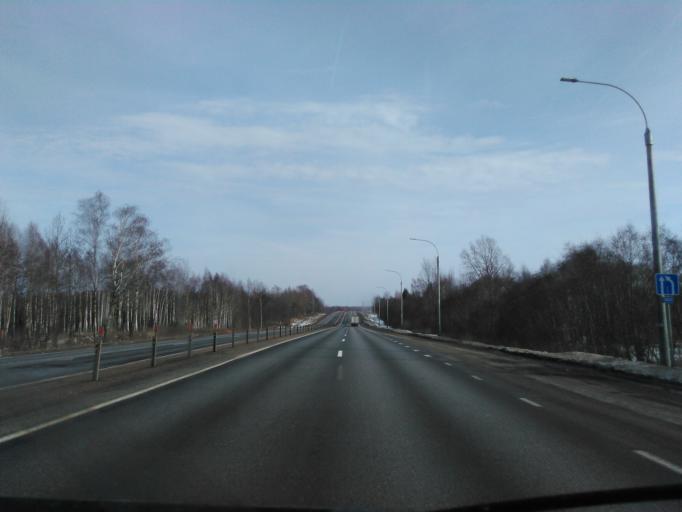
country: BY
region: Vitebsk
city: Dubrowna
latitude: 54.6887
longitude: 30.8755
